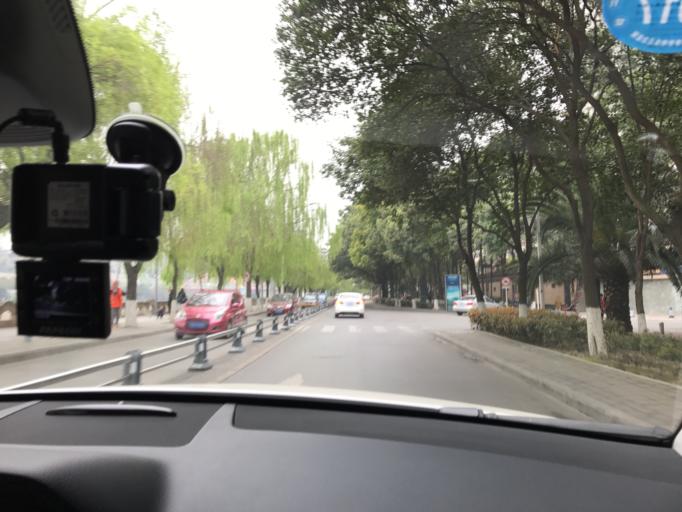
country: CN
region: Sichuan
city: Mianyang
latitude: 31.4567
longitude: 104.7217
